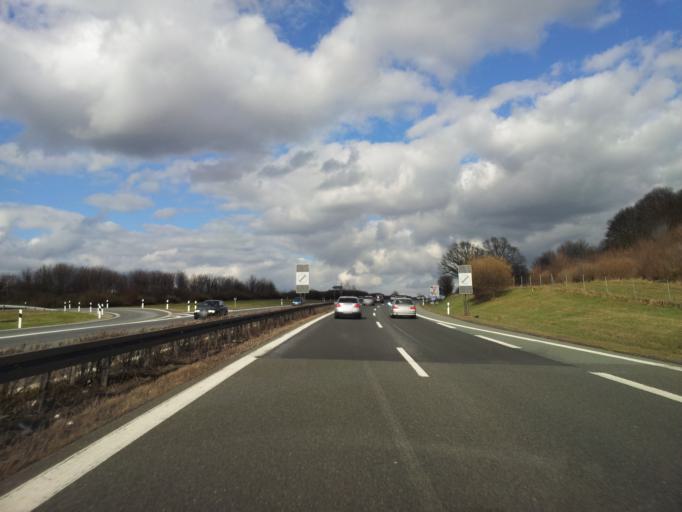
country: DE
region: Saxony
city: Neuensalz
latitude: 50.5024
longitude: 12.2043
